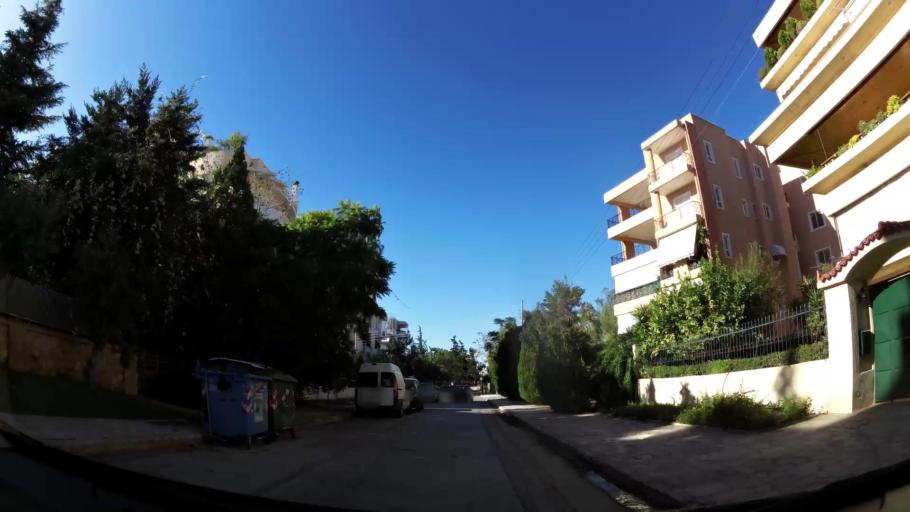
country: GR
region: Attica
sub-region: Nomarchia Athinas
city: Glyfada
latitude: 37.8476
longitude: 23.7614
